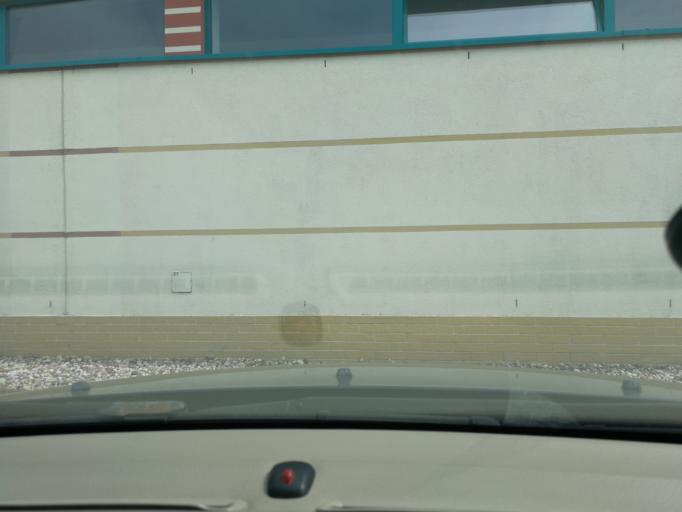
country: PL
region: Masovian Voivodeship
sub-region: Powiat zyrardowski
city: Mszczonow
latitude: 51.9785
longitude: 20.5253
